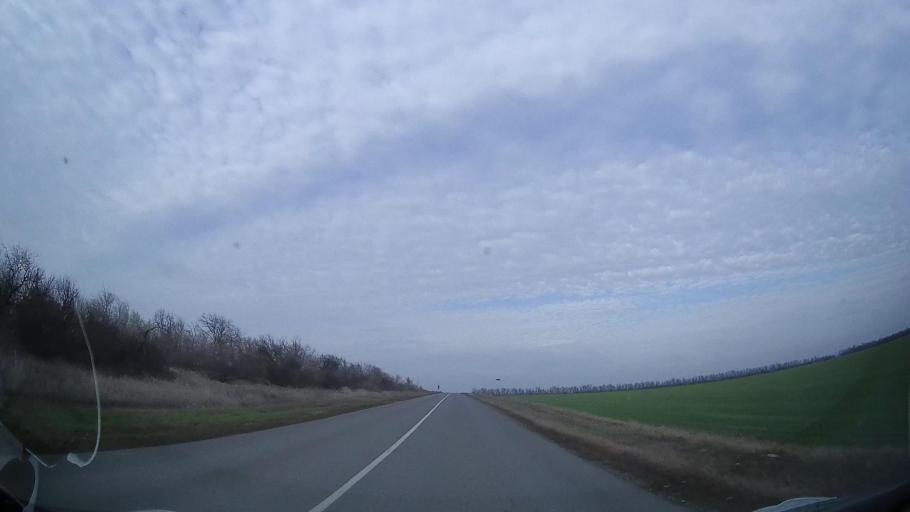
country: RU
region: Rostov
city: Zernograd
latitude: 46.9064
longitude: 40.3390
